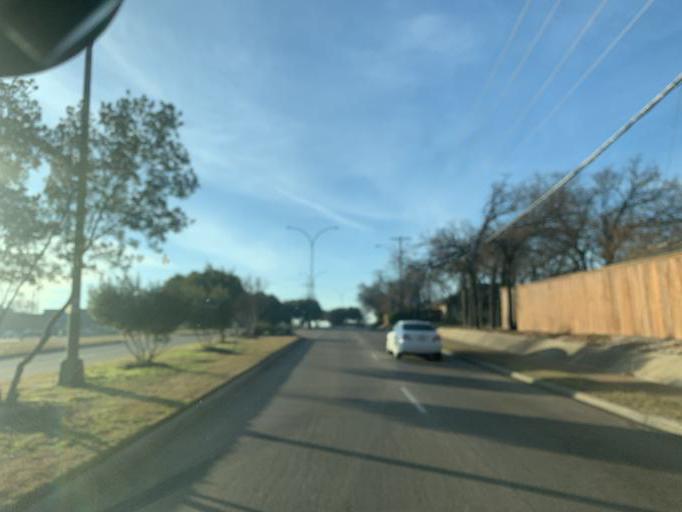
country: US
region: Texas
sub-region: Tarrant County
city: Arlington
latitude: 32.7669
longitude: -97.0738
